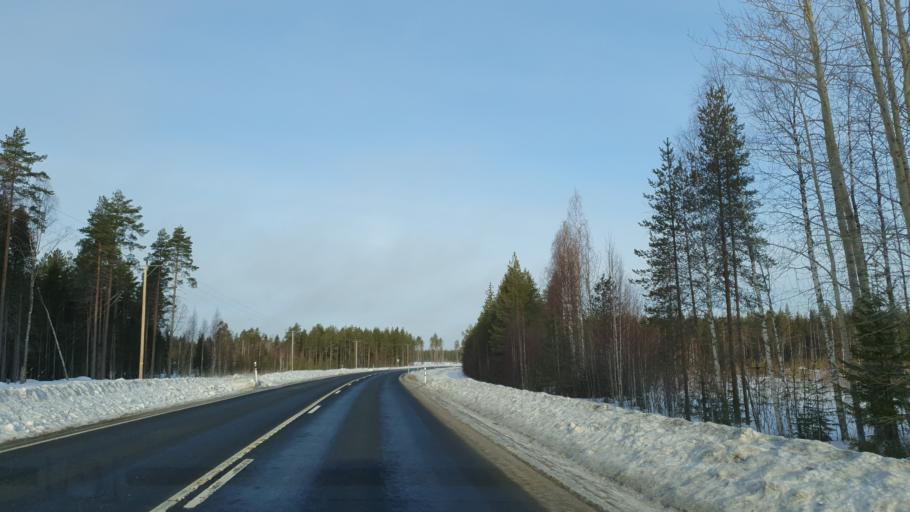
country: FI
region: North Karelia
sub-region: Pielisen Karjala
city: Valtimo
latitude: 64.0827
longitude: 28.9931
